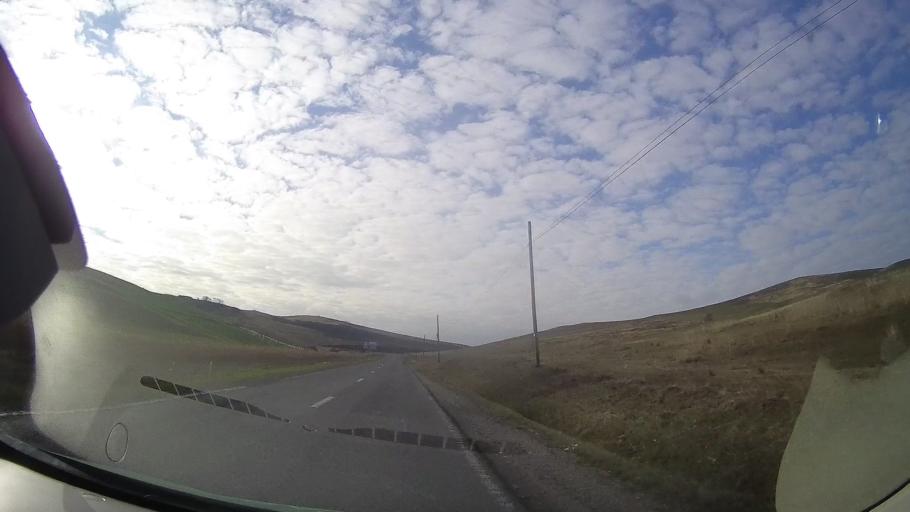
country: RO
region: Cluj
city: Jucu Herghelia
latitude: 46.8120
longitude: 23.8103
